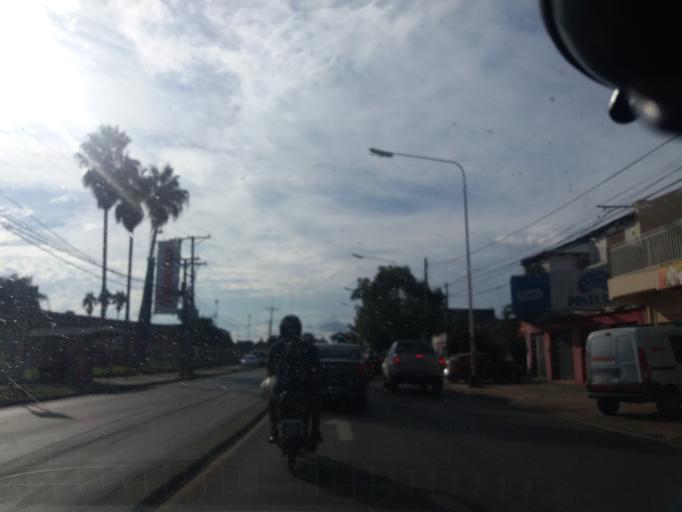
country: AR
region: Corrientes
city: Corrientes
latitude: -27.4840
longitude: -58.8250
